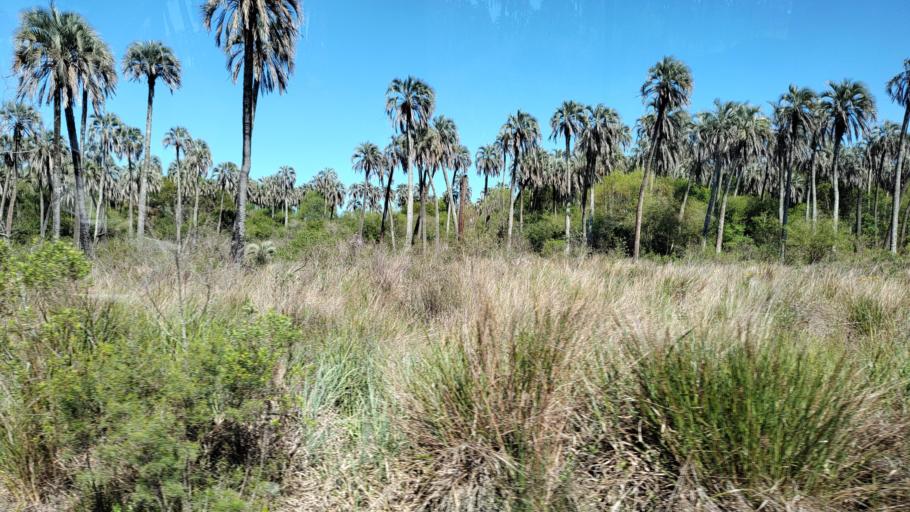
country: AR
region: Entre Rios
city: Ubajay
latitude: -31.8806
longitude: -58.2360
